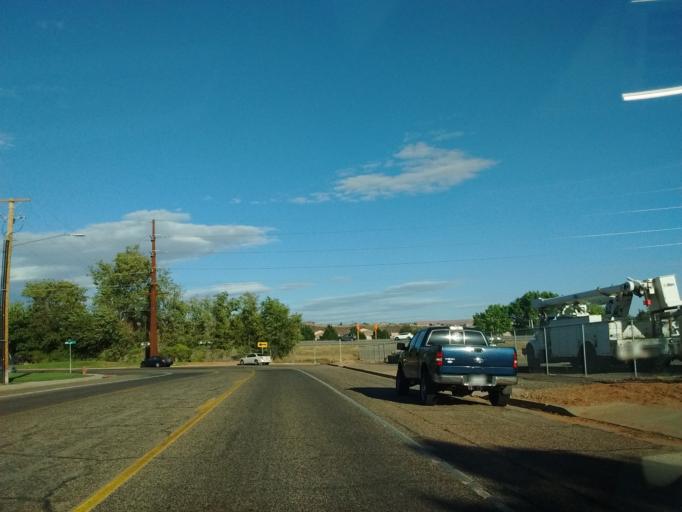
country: US
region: Utah
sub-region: Washington County
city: Saint George
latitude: 37.1013
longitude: -113.5629
